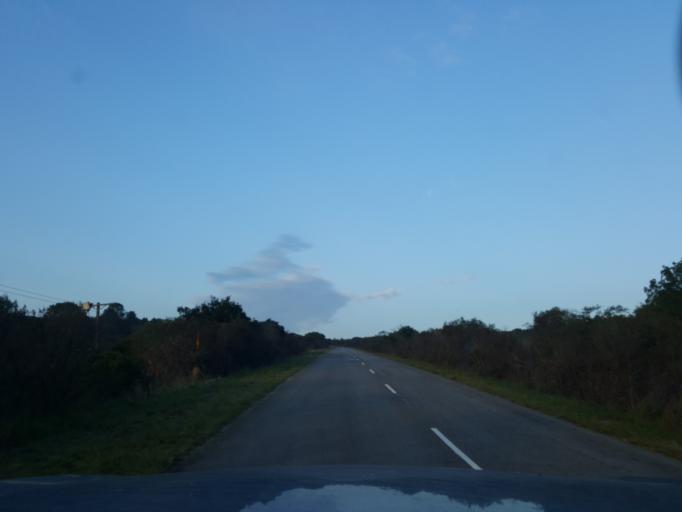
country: ZA
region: Eastern Cape
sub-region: Cacadu District Municipality
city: Grahamstown
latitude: -33.4623
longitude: 26.4896
